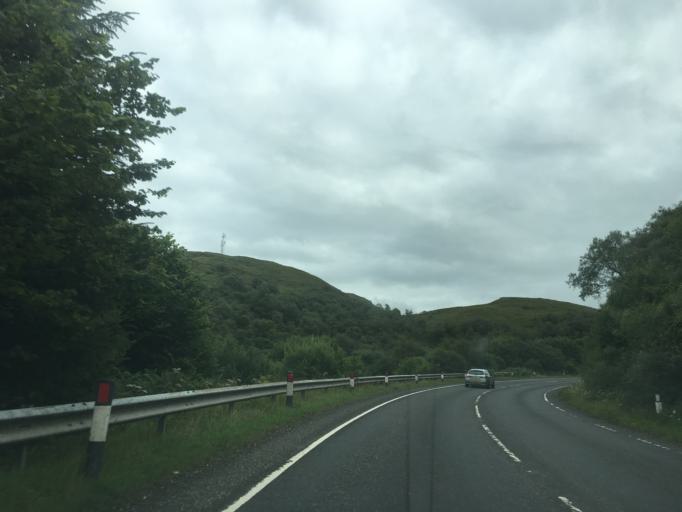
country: GB
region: Scotland
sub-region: Argyll and Bute
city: Oban
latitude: 56.3082
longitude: -5.4673
